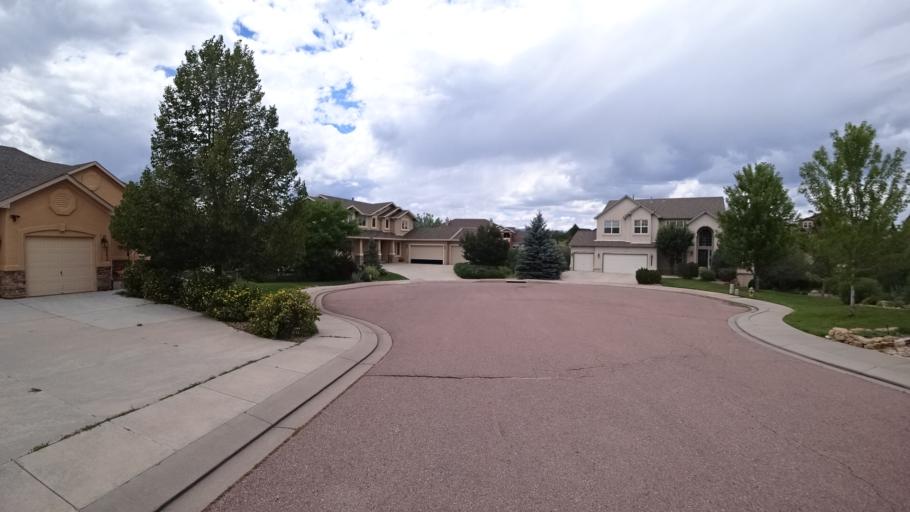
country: US
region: Colorado
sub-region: El Paso County
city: Gleneagle
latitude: 39.0197
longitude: -104.8053
